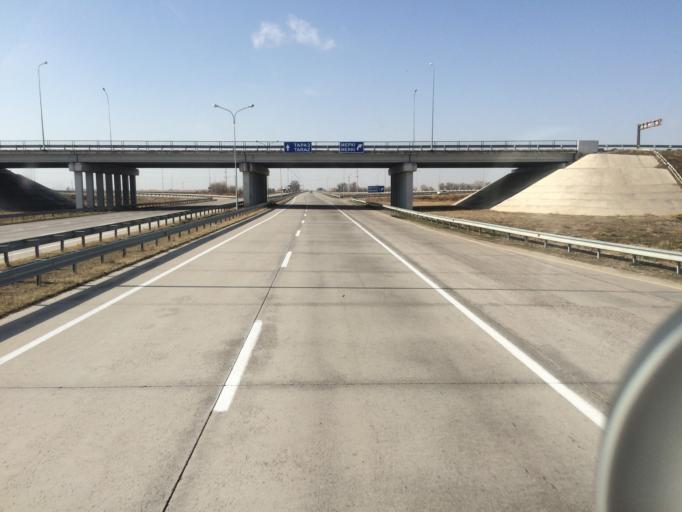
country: KZ
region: Zhambyl
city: Oytal
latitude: 42.9286
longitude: 73.2434
